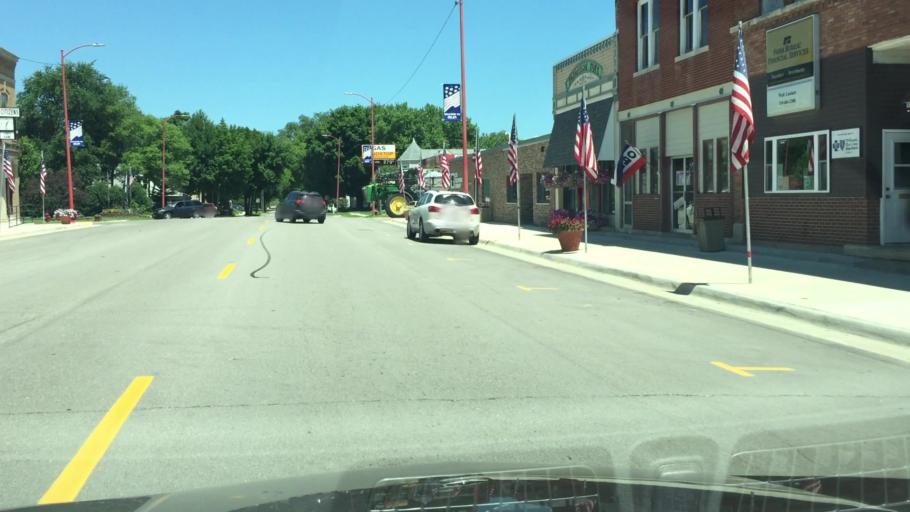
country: US
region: Iowa
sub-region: Cedar County
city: Mechanicsville
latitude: 41.9974
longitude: -91.1419
